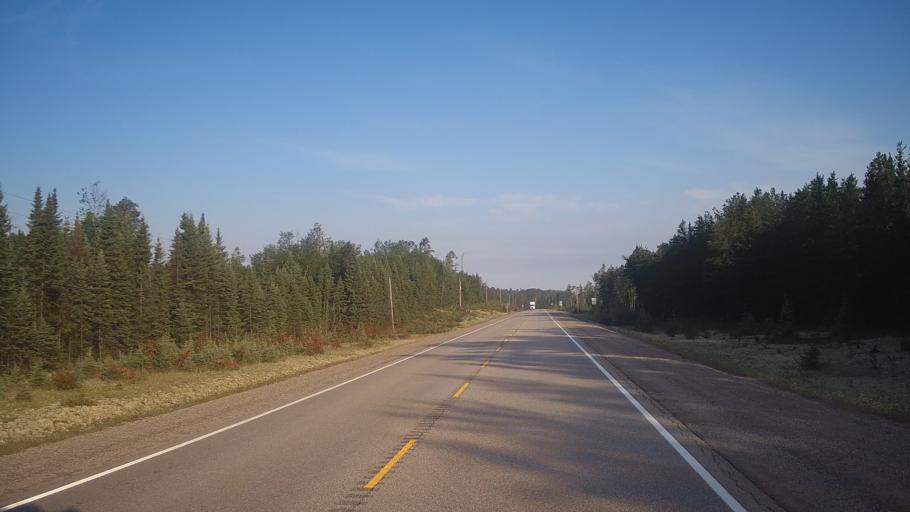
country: CA
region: Ontario
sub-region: Rainy River District
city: Atikokan
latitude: 49.3489
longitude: -91.5100
